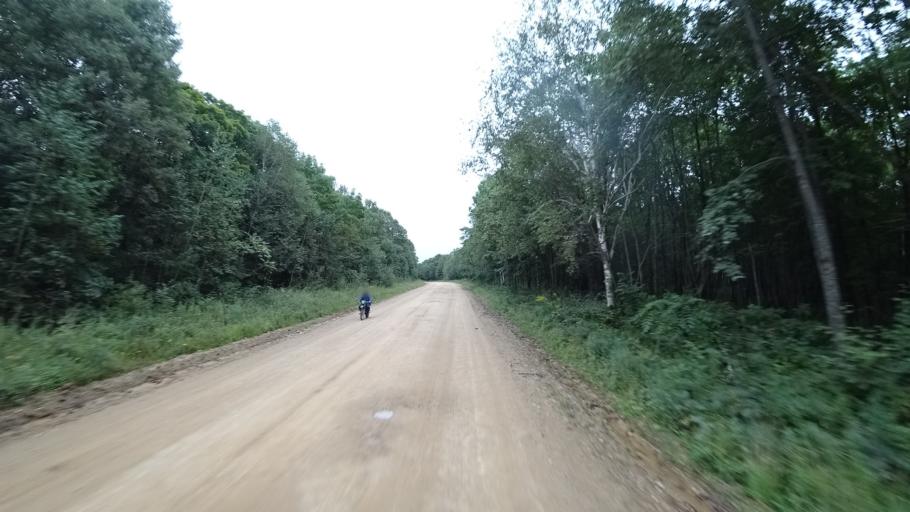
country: RU
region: Primorskiy
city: Rettikhovka
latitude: 44.1839
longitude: 132.8198
